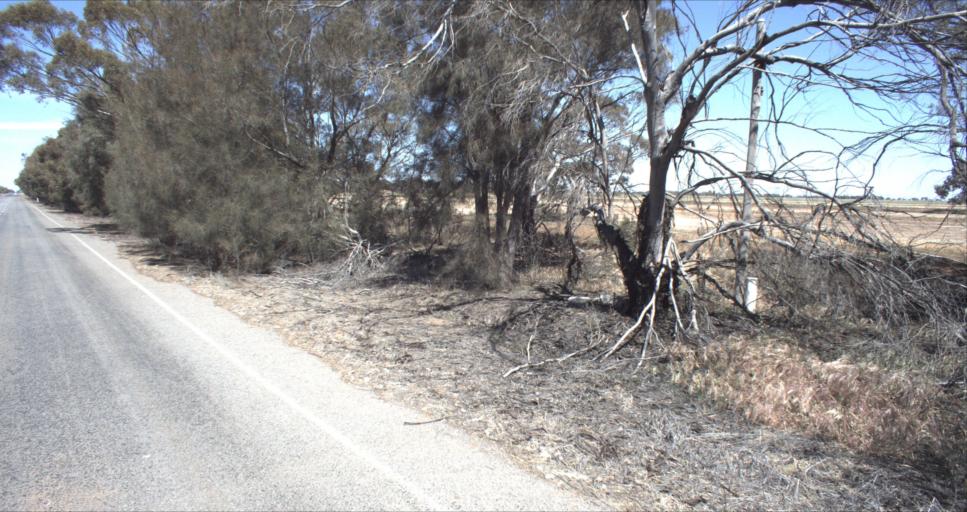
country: AU
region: New South Wales
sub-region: Leeton
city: Leeton
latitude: -34.4688
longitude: 146.2927
